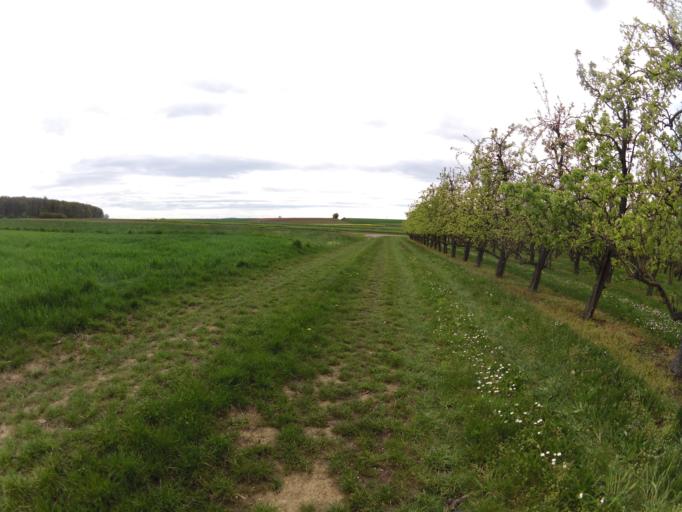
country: DE
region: Bavaria
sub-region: Regierungsbezirk Unterfranken
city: Prosselsheim
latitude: 49.8652
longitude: 10.1518
